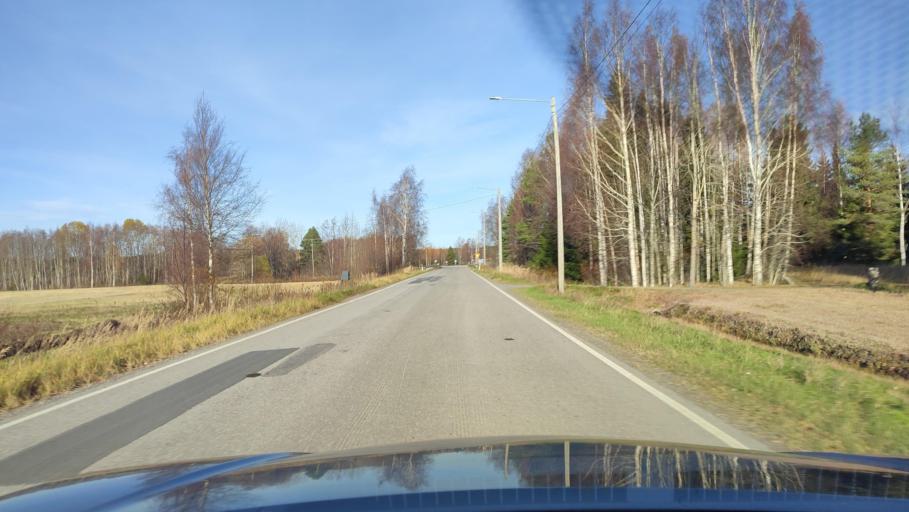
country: FI
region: Southern Ostrobothnia
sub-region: Suupohja
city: Teuva
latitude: 62.4585
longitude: 21.6049
